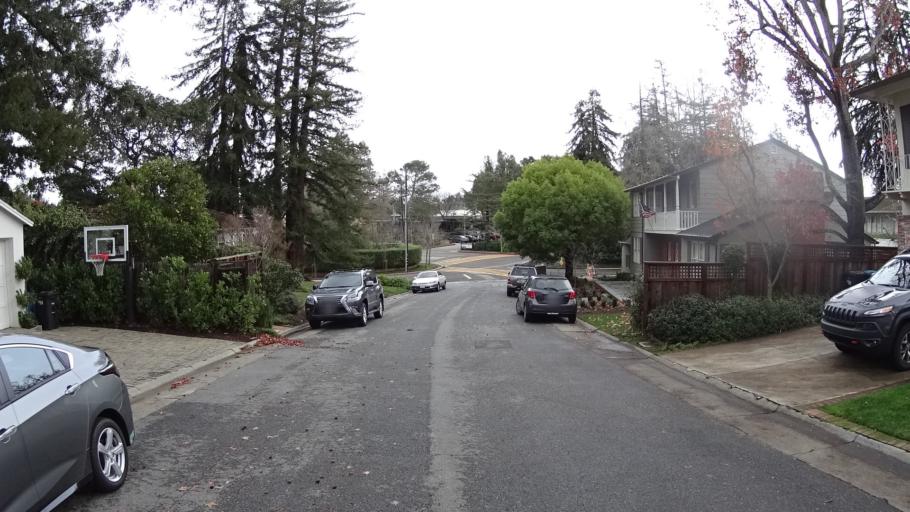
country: US
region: California
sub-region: San Mateo County
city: San Mateo
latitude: 37.5695
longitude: -122.3443
